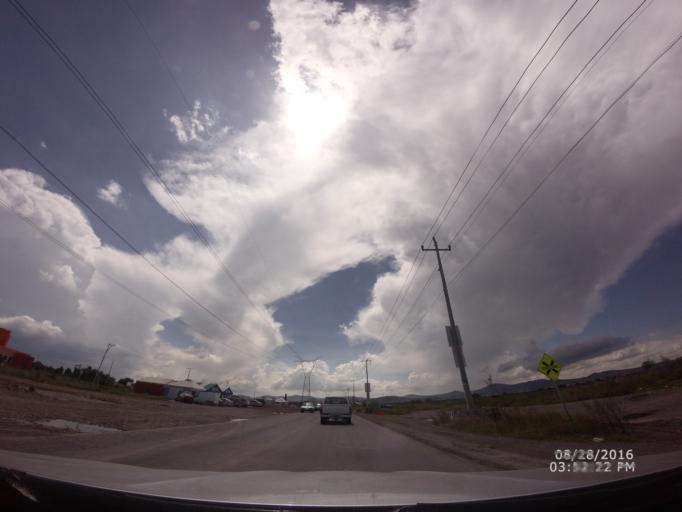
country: MX
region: Hidalgo
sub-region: Mineral de la Reforma
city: Los Tuzos
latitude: 20.0364
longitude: -98.7475
